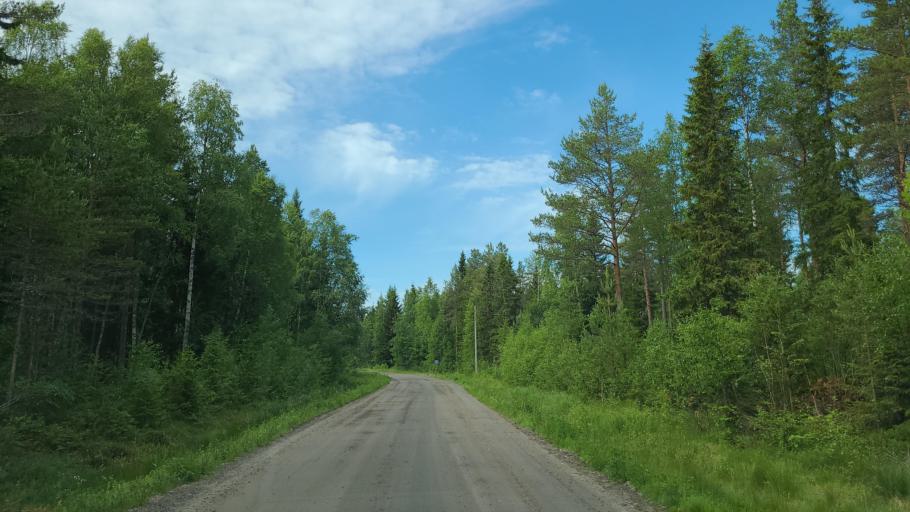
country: SE
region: Vaesterbotten
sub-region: Robertsfors Kommun
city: Robertsfors
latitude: 64.1644
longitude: 20.9705
